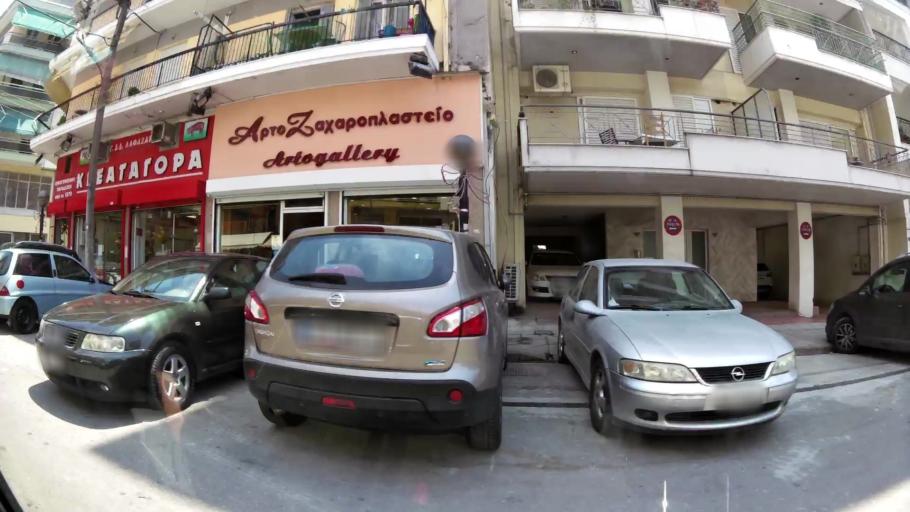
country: GR
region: Central Macedonia
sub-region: Nomos Thessalonikis
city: Thessaloniki
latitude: 40.6499
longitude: 22.9327
